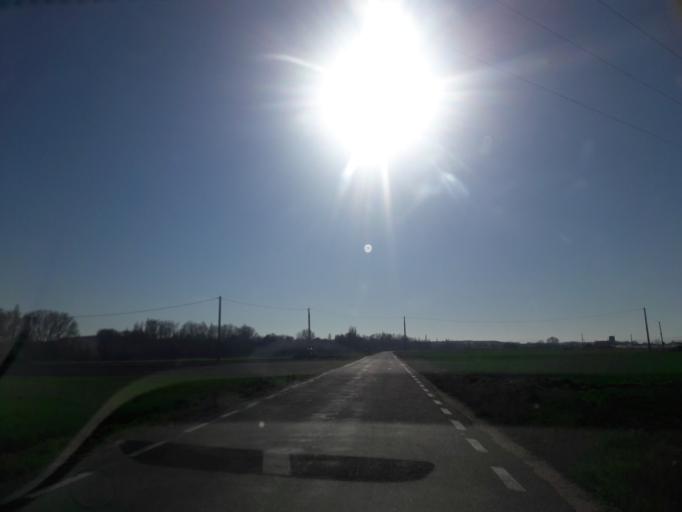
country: ES
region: Castille and Leon
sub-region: Provincia de Salamanca
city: Tordillos
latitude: 40.8608
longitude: -5.3640
